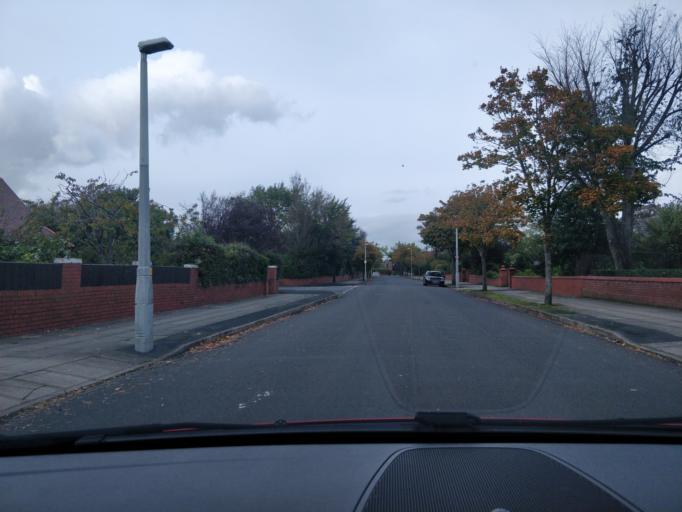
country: GB
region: England
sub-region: Sefton
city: Southport
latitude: 53.6256
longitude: -3.0186
